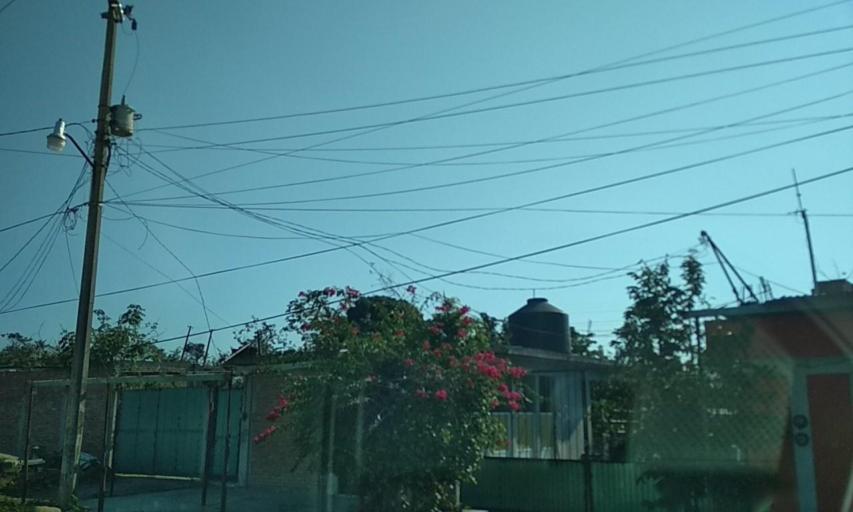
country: MX
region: Veracruz
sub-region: Papantla
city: El Chote
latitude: 20.4082
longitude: -97.3460
